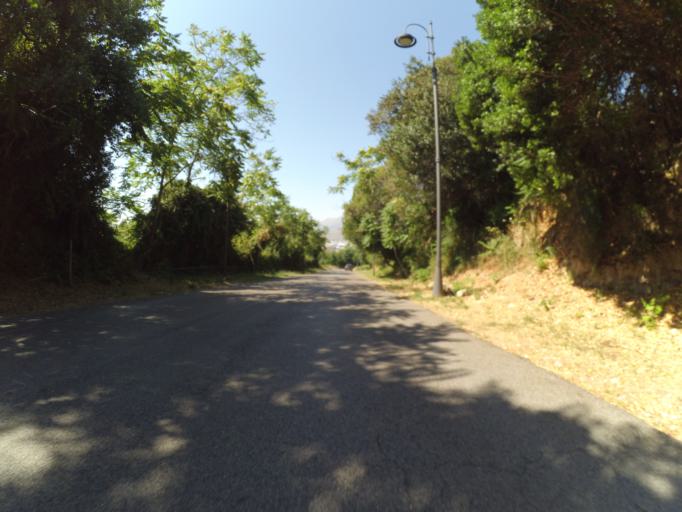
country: IT
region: Latium
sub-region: Provincia di Latina
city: Gaeta
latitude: 41.2098
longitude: 13.5728
